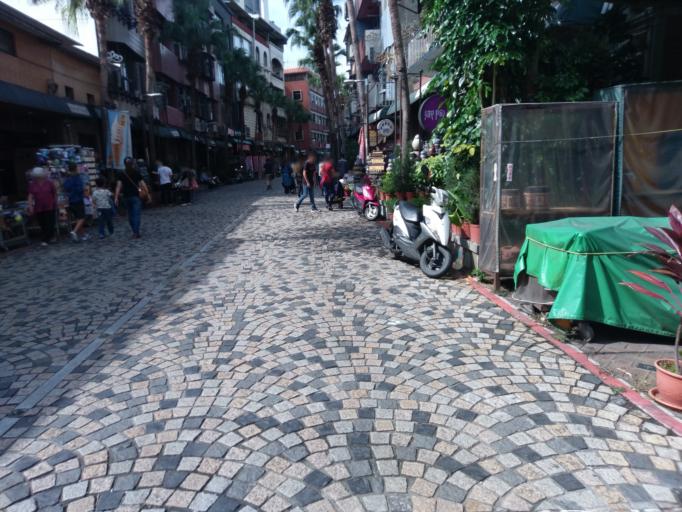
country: TW
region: Taiwan
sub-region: Taoyuan
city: Taoyuan
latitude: 24.9510
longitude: 121.3483
